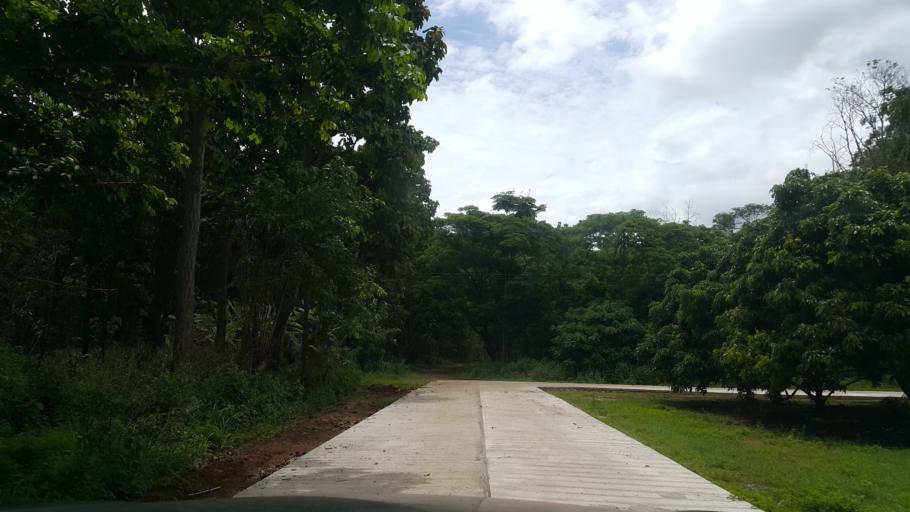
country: TH
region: Chiang Mai
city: Mae Taeng
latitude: 19.1738
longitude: 98.9570
